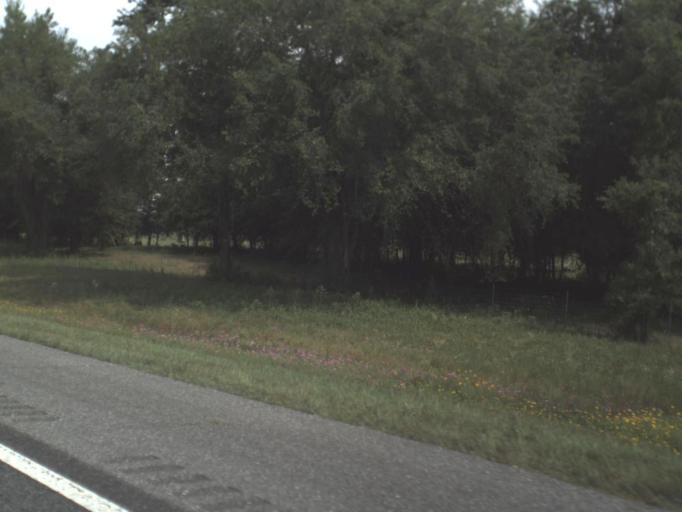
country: US
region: Florida
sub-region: Suwannee County
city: Wellborn
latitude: 30.2922
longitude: -82.8801
